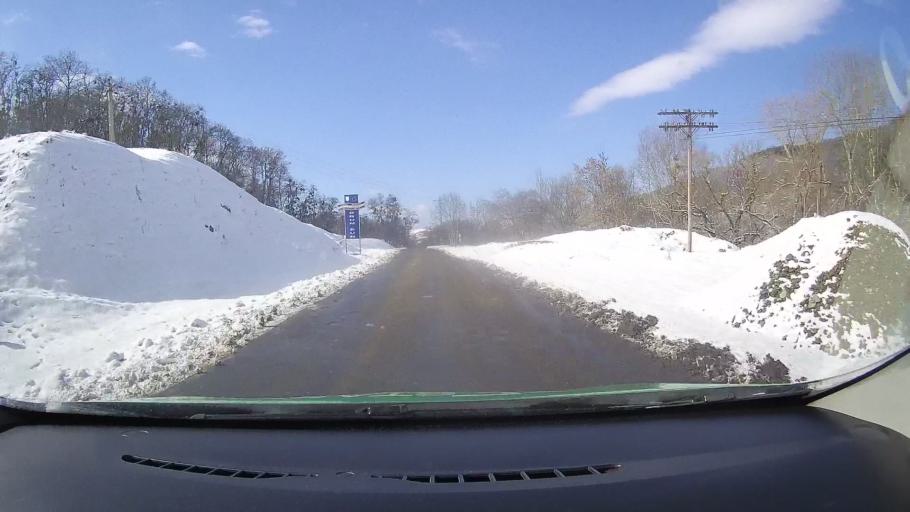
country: RO
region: Sibiu
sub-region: Comuna Mosna
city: Mosna
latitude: 46.0206
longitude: 24.4014
